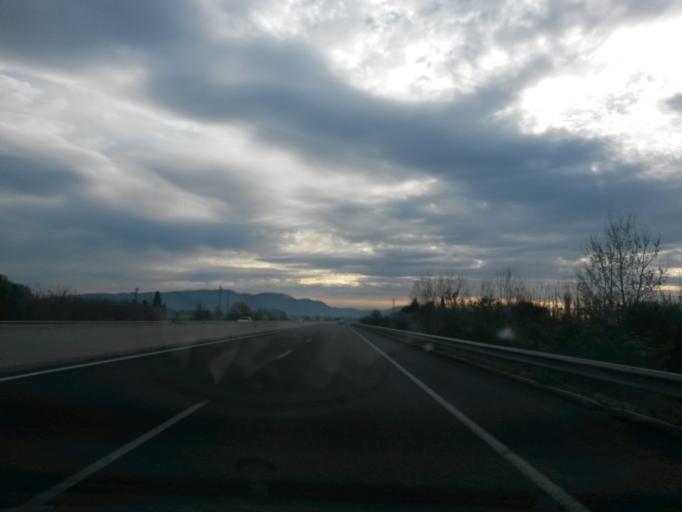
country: ES
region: Catalonia
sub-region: Provincia de Girona
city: Vila-sacra
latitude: 42.2692
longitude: 3.0135
